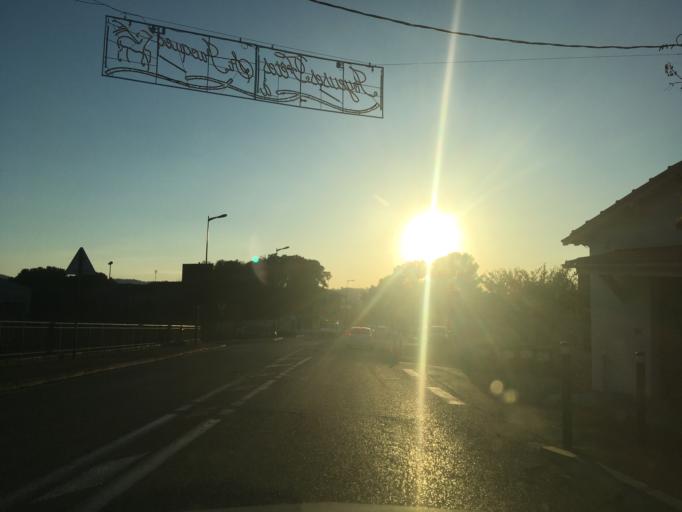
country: FR
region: Provence-Alpes-Cote d'Azur
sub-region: Departement des Alpes-Maritimes
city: Grasse
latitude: 43.6414
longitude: 6.9111
